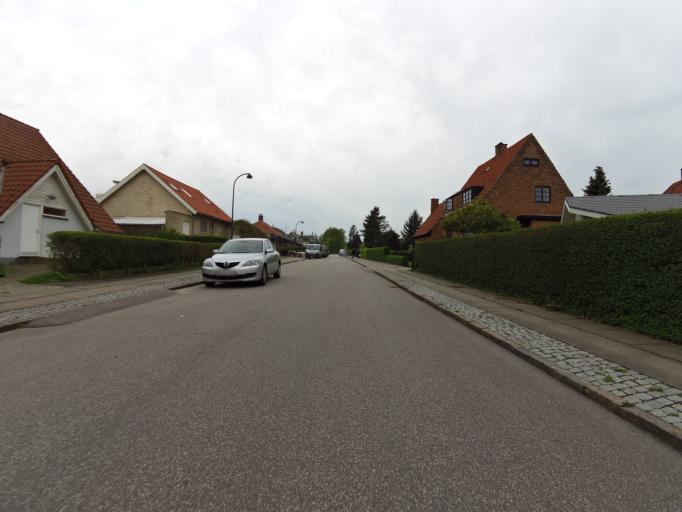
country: DK
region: Capital Region
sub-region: Lyngby-Tarbaek Kommune
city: Kongens Lyngby
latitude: 55.7374
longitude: 12.5276
